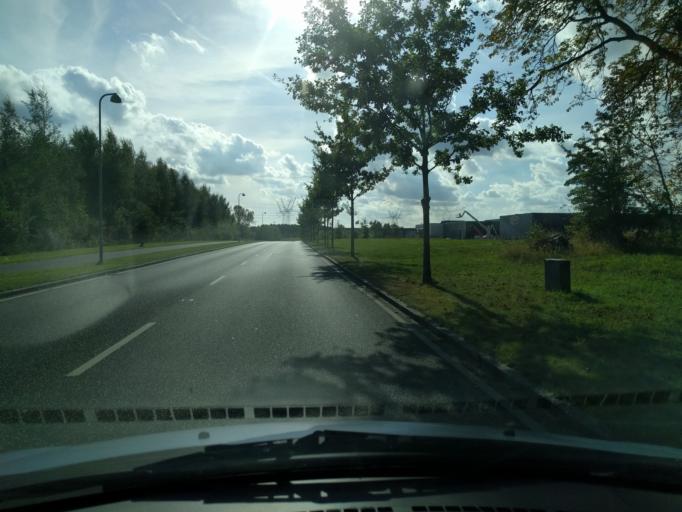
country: DK
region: South Denmark
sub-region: Odense Kommune
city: Neder Holluf
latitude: 55.3665
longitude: 10.5016
